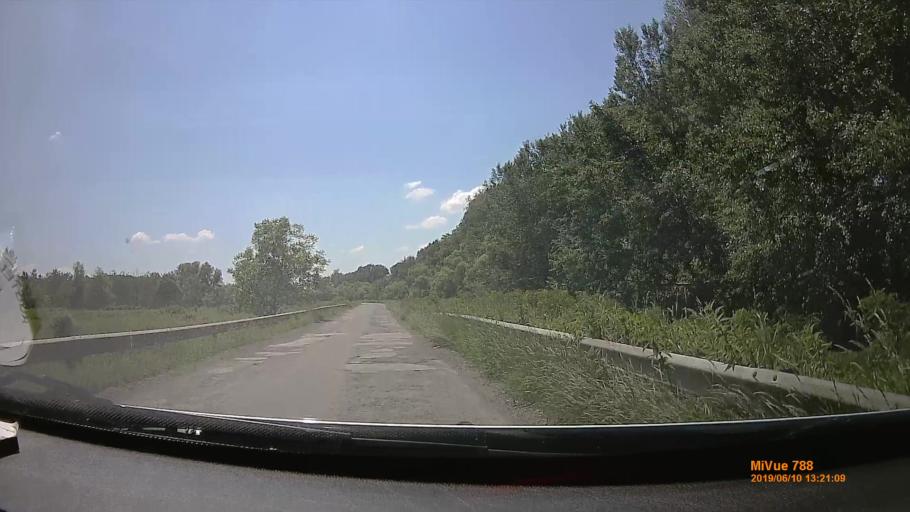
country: HU
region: Borsod-Abauj-Zemplen
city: Tiszaluc
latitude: 48.0375
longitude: 21.0780
